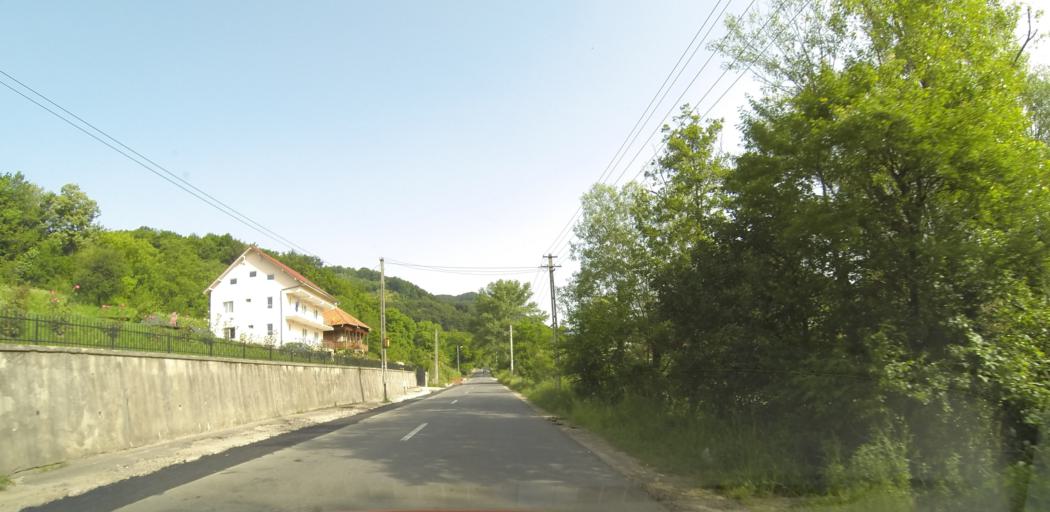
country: RO
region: Valcea
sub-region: Oras Baile Olanesti
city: Olanesti
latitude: 45.1844
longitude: 24.2550
